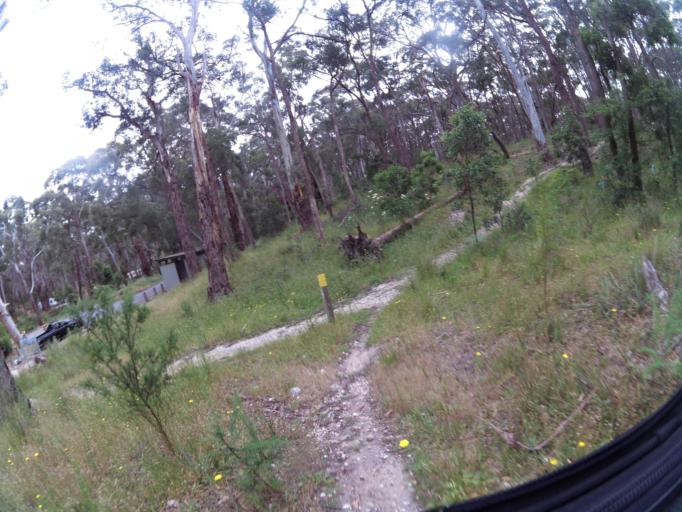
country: AU
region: Victoria
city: Brown Hill
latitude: -37.4630
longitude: 143.9046
